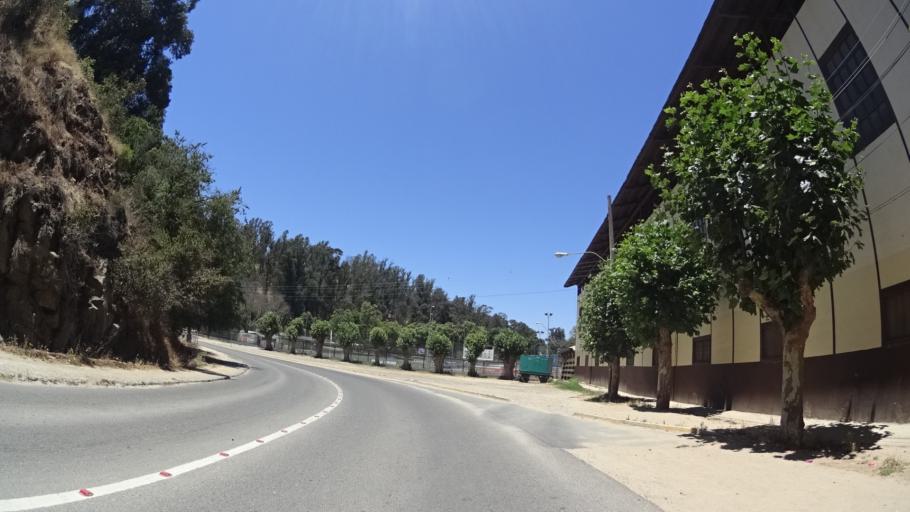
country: CL
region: Valparaiso
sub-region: Provincia de Valparaiso
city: Vina del Mar
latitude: -33.0208
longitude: -71.5371
